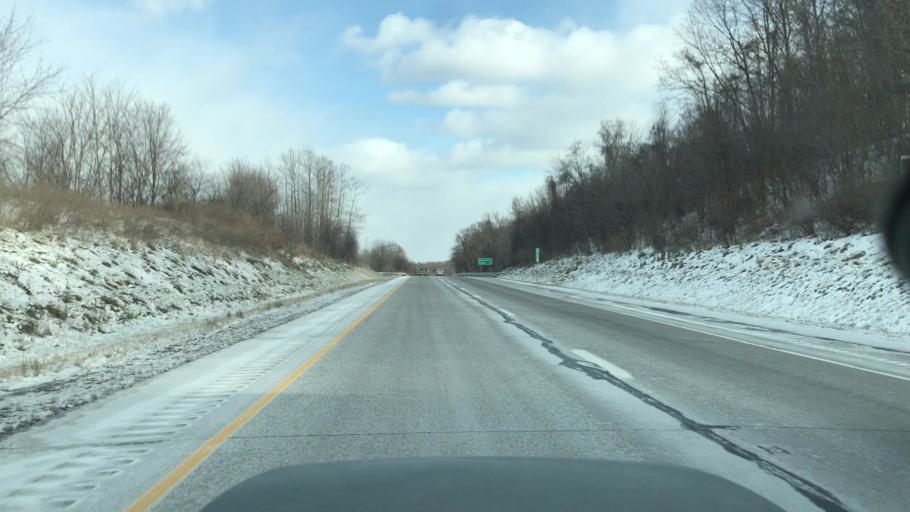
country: US
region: Pennsylvania
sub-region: Jefferson County
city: Brookville
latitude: 41.1859
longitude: -79.1859
